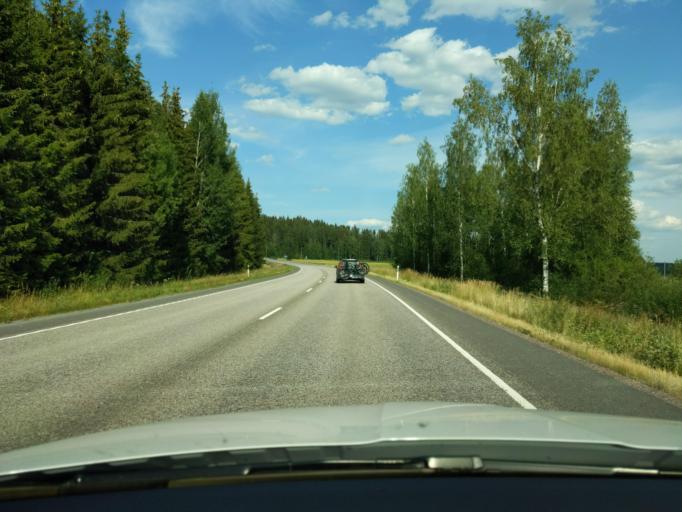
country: FI
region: Paijanne Tavastia
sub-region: Lahti
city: Nastola
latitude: 60.9234
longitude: 26.0498
